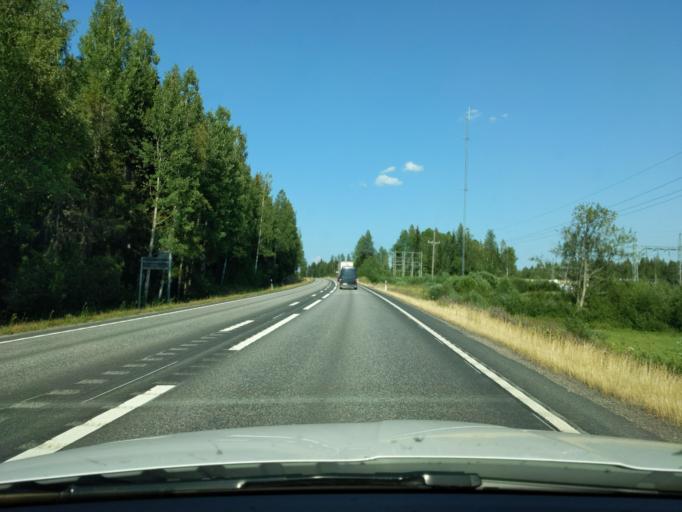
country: FI
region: Paijanne Tavastia
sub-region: Lahti
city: Jaervelae
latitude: 60.9117
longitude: 25.3452
